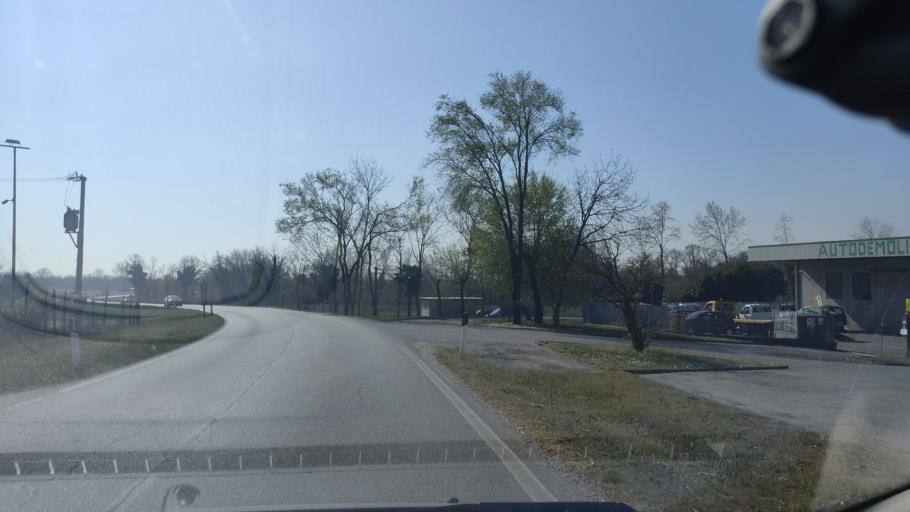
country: IT
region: Friuli Venezia Giulia
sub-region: Provincia di Pordenone
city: Budoia
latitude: 46.0357
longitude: 12.5484
